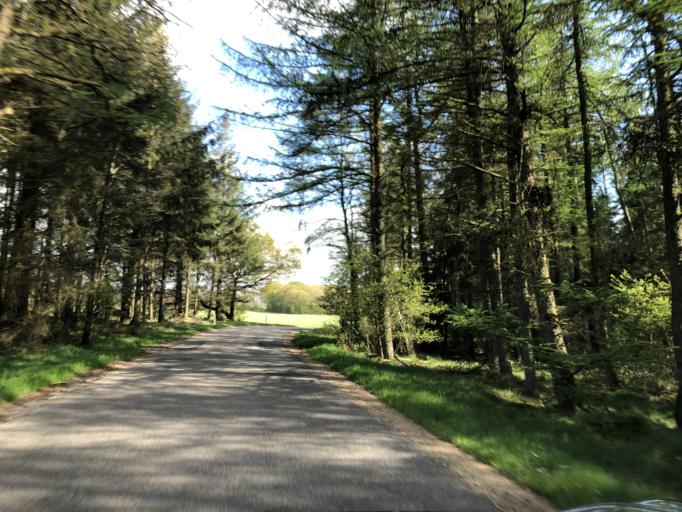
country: DK
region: Central Jutland
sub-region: Herning Kommune
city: Avlum
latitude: 56.2986
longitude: 8.7008
